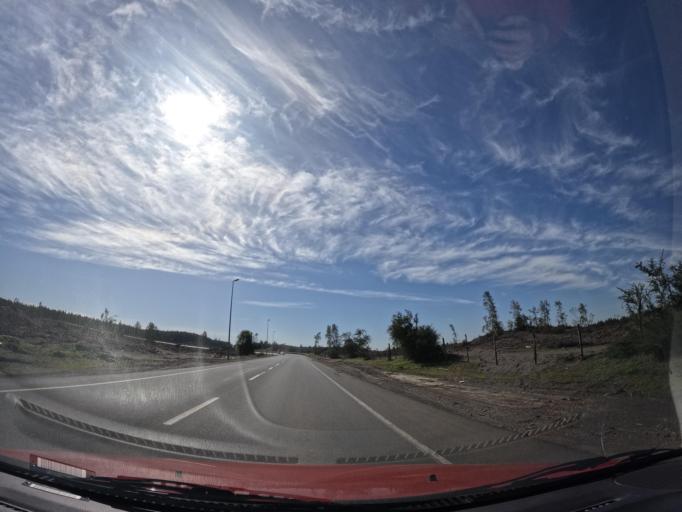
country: CL
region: Biobio
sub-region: Provincia de Biobio
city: Cabrero
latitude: -36.9355
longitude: -72.3448
